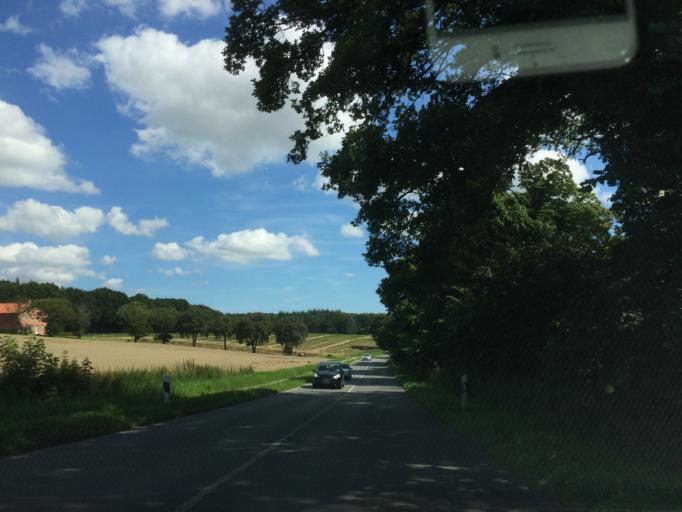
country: DE
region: Schleswig-Holstein
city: Malente
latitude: 54.1613
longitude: 10.5859
